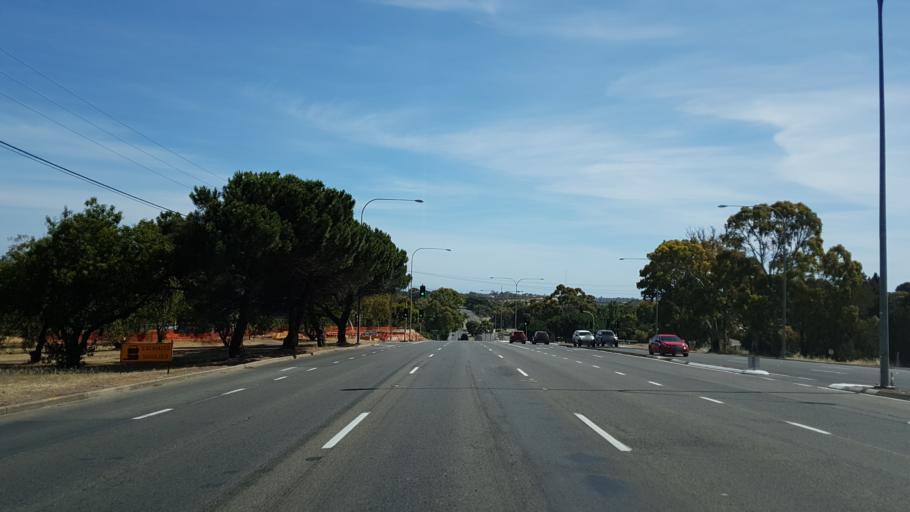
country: AU
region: South Australia
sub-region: Marion
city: Trott Park
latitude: -35.0747
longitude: 138.5512
